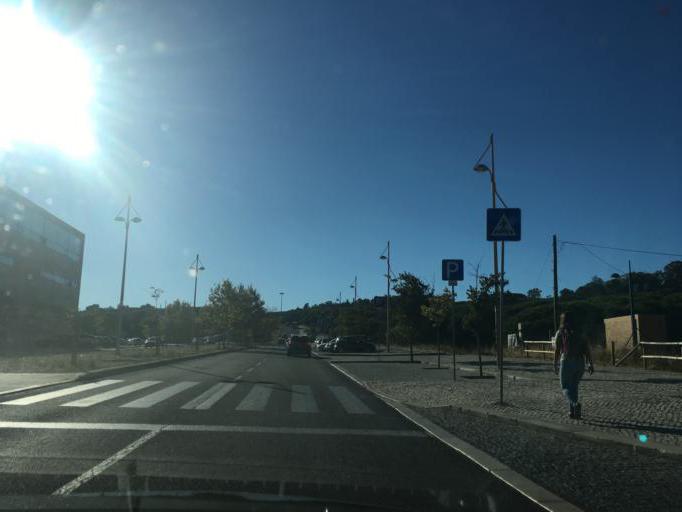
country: PT
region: Lisbon
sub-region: Oeiras
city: Alges
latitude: 38.7139
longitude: -9.1969
